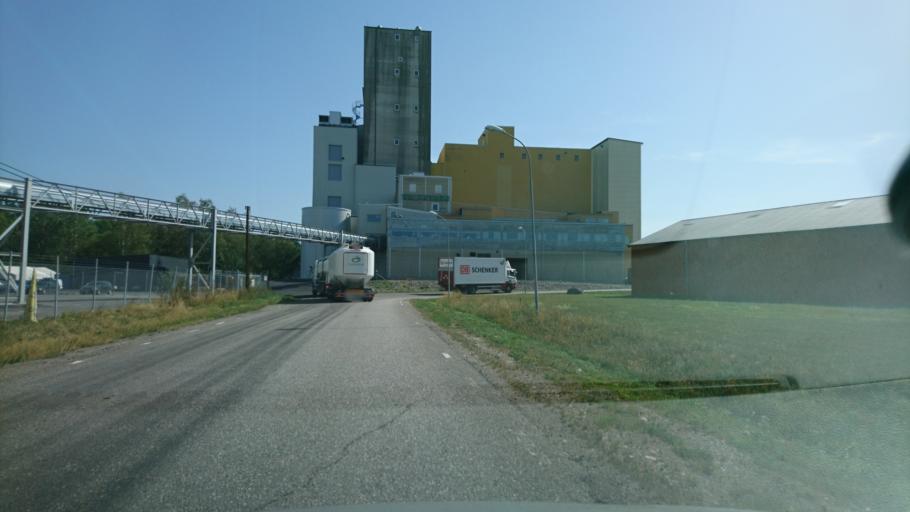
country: SE
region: Soedermanland
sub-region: Strangnas Kommun
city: Strangnas
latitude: 59.3531
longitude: 17.0520
